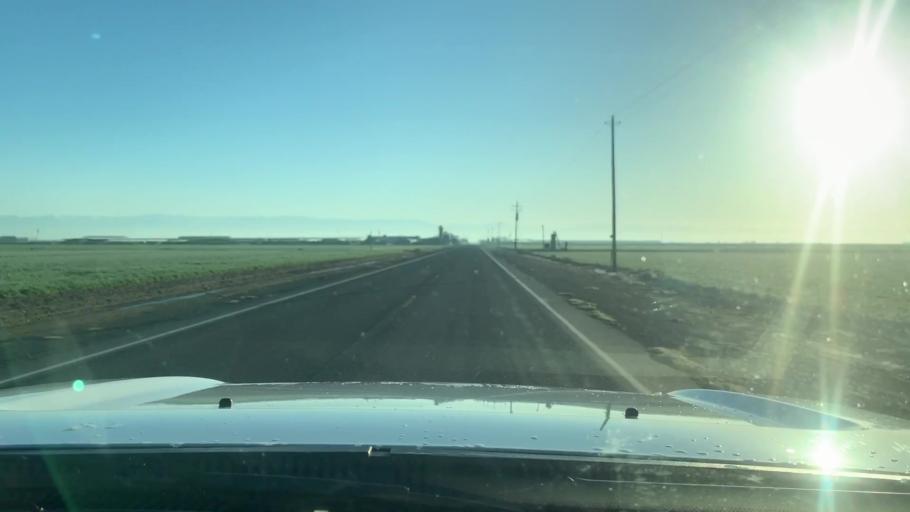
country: US
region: California
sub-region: Kings County
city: Corcoran
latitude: 36.2111
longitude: -119.5533
